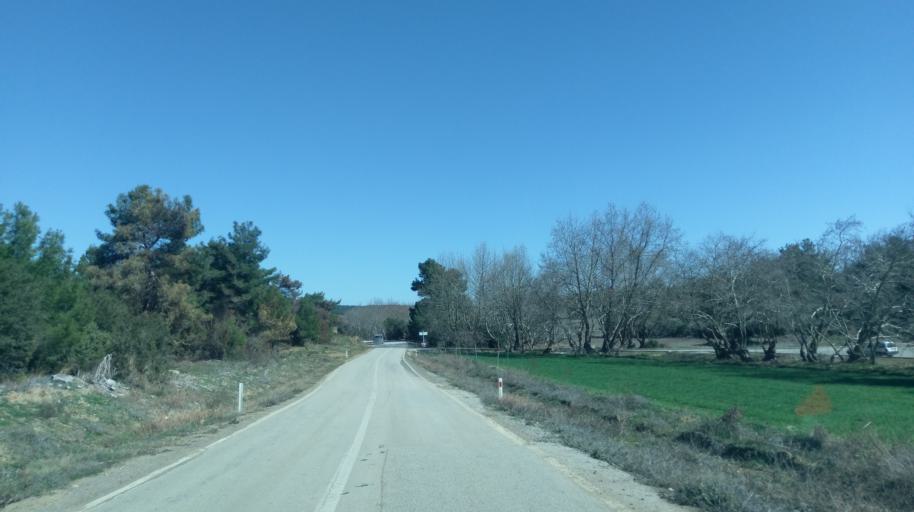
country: TR
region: Canakkale
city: Eceabat
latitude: 40.1227
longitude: 26.2602
